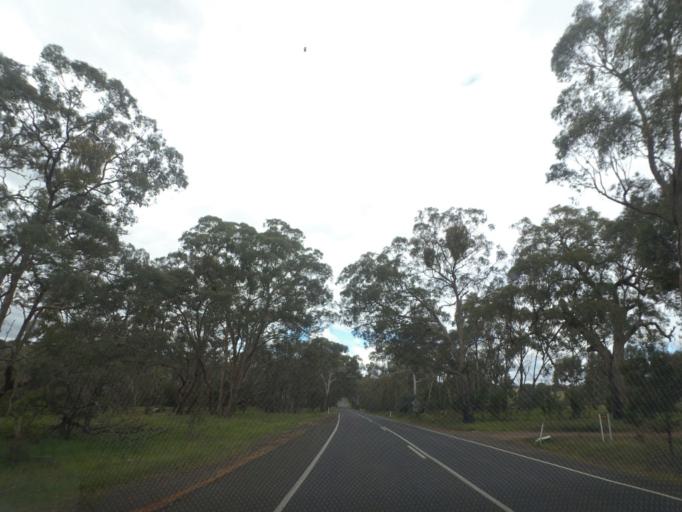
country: AU
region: Victoria
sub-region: Hume
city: Craigieburn
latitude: -37.3970
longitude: 144.9261
